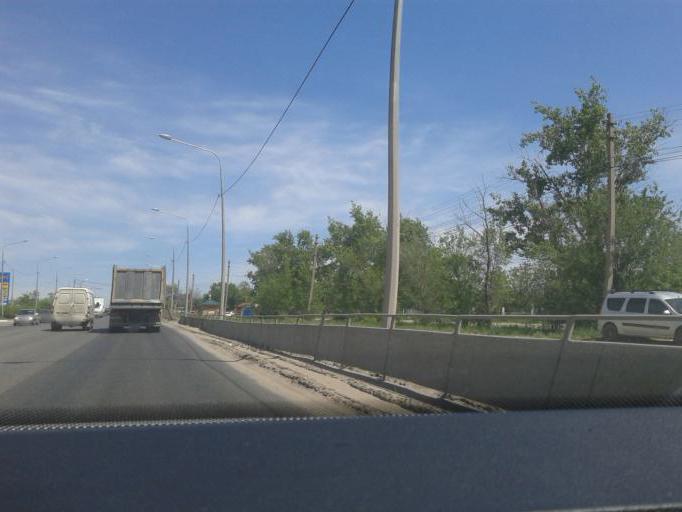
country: RU
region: Volgograd
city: Gorodishche
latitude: 48.7788
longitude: 44.5200
